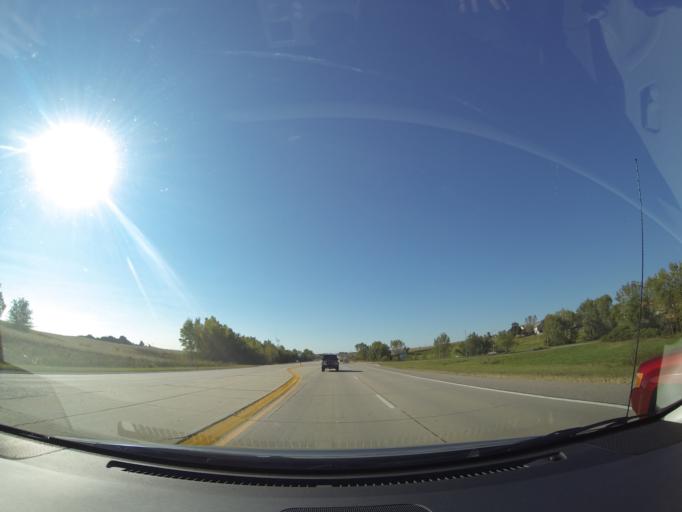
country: US
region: Nebraska
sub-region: Sarpy County
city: Gretna
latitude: 41.1221
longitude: -96.2532
